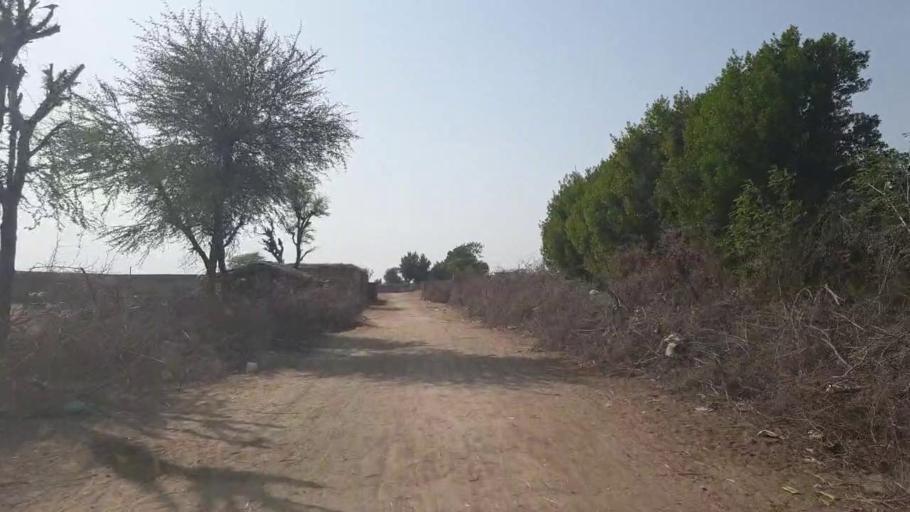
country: PK
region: Sindh
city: Dhoro Naro
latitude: 25.4448
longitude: 69.5488
